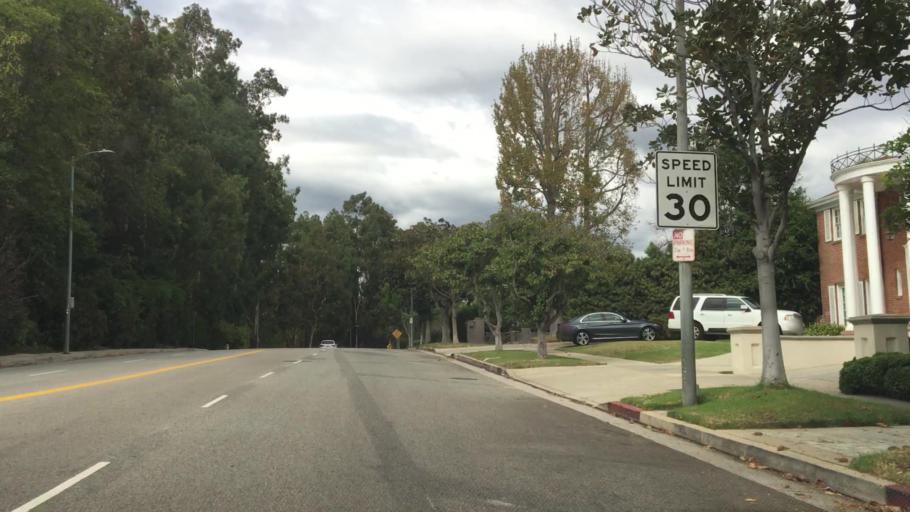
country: US
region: California
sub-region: Los Angeles County
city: Westwood, Los Angeles
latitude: 34.0746
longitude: -118.4382
